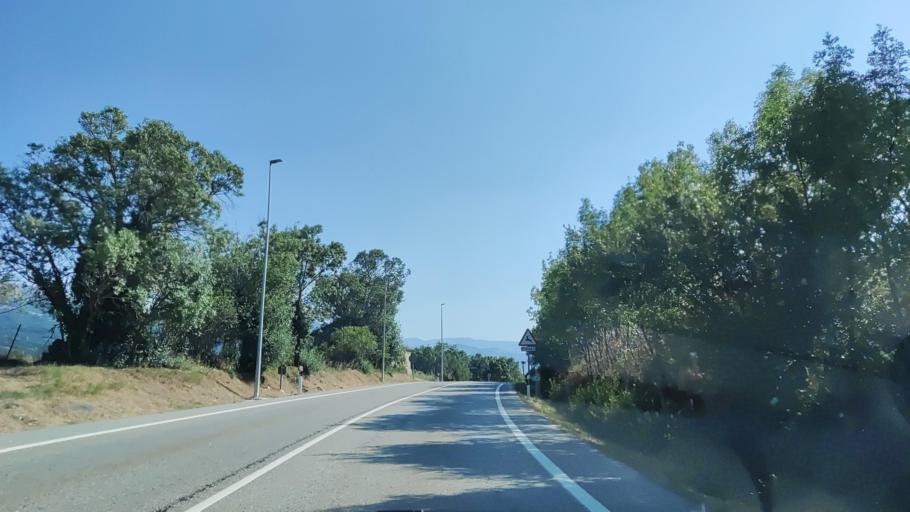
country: ES
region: Madrid
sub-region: Provincia de Madrid
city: Lozoya
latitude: 40.9486
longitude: -3.7925
